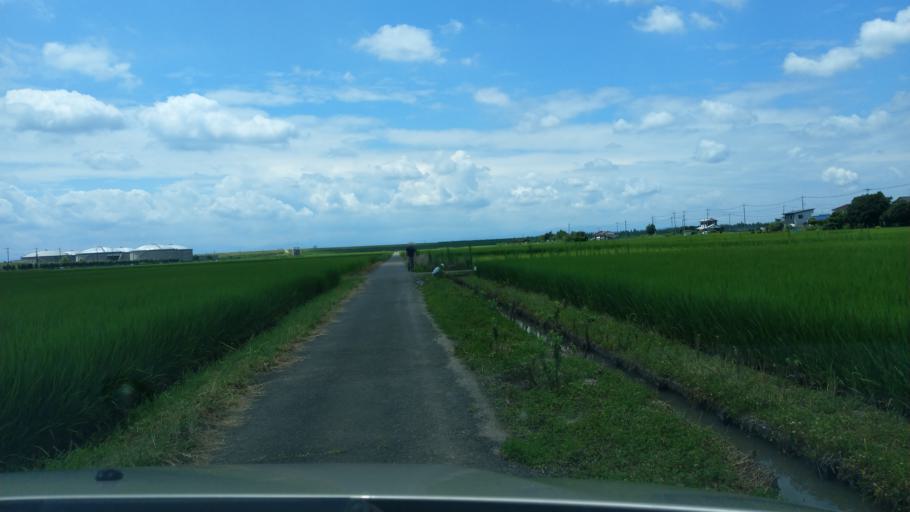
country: JP
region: Saitama
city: Yono
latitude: 35.8812
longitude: 139.5946
